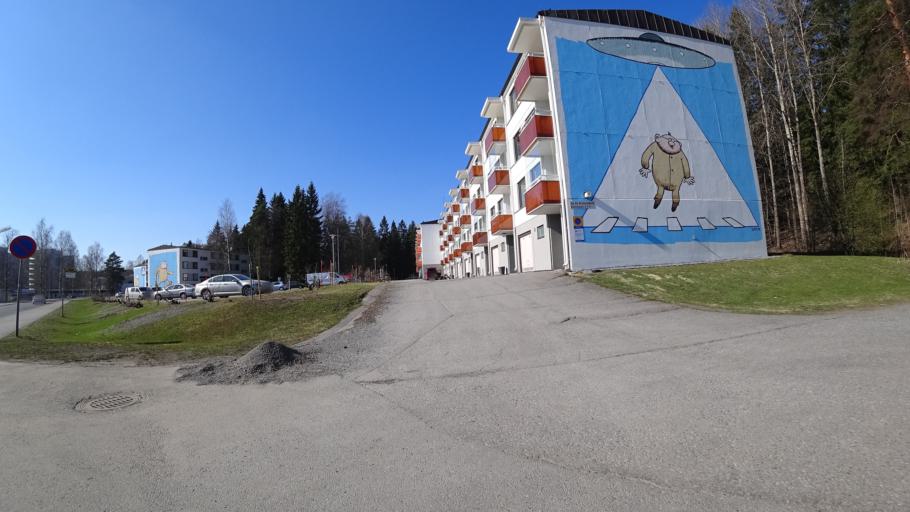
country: FI
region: Pirkanmaa
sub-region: Tampere
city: Pirkkala
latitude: 61.5040
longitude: 23.6368
